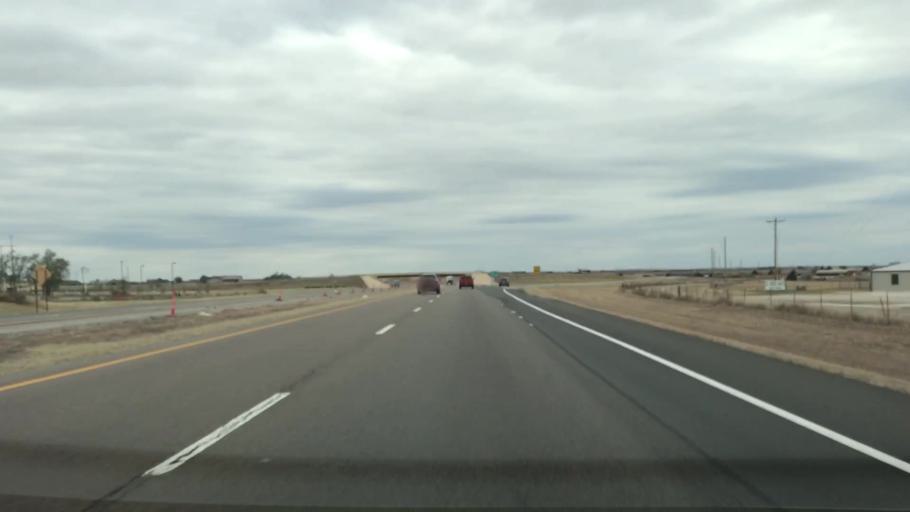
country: US
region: Oklahoma
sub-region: Washita County
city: Burns Flat
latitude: 35.4240
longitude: -99.2707
